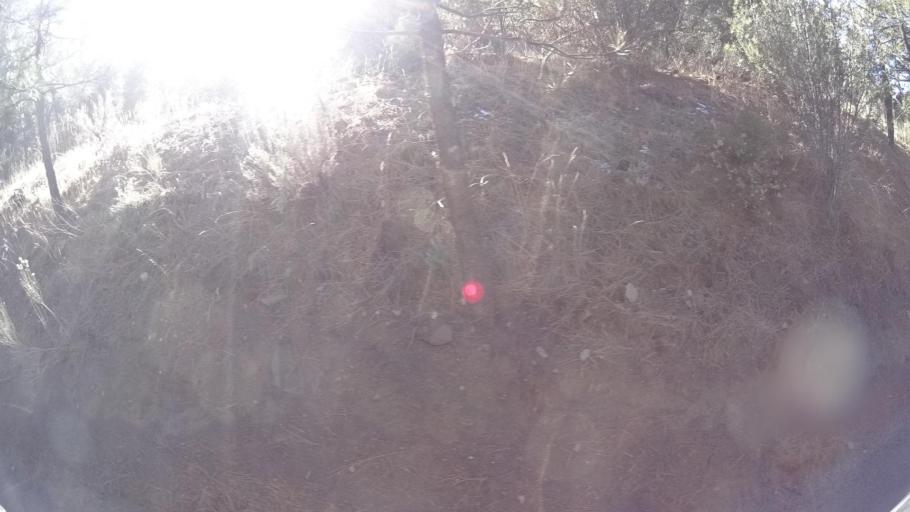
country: US
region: California
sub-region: Kern County
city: Pine Mountain Club
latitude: 34.8491
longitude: -119.0985
